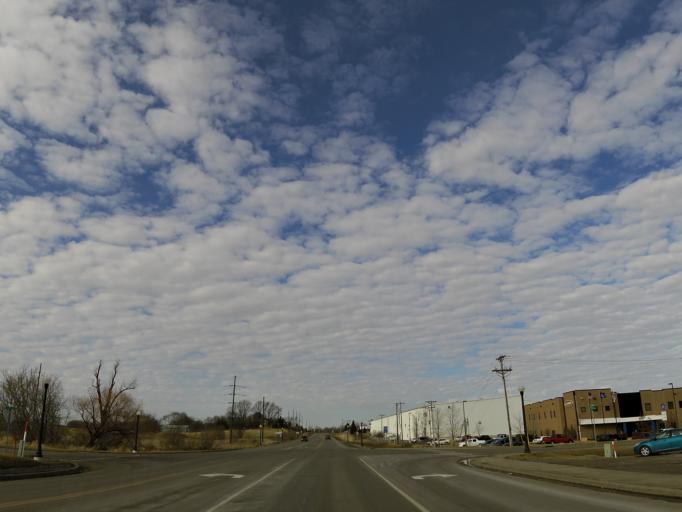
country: US
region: Minnesota
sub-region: Le Sueur County
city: New Prague
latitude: 44.5496
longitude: -93.5847
